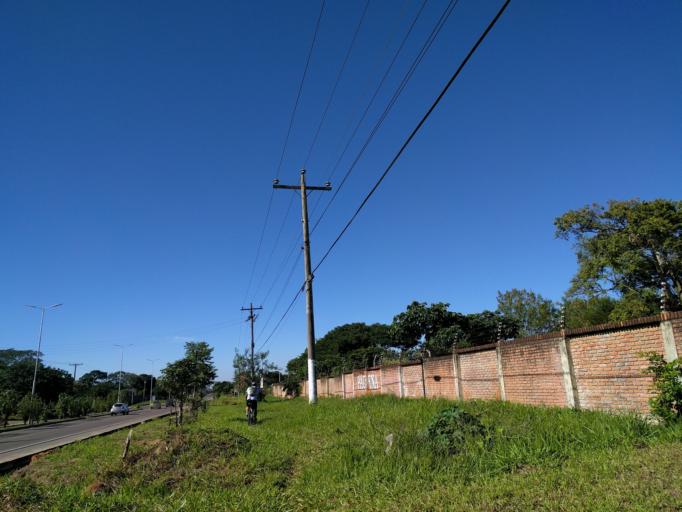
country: BO
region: Santa Cruz
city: Santa Rita
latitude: -17.8755
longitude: -63.2800
